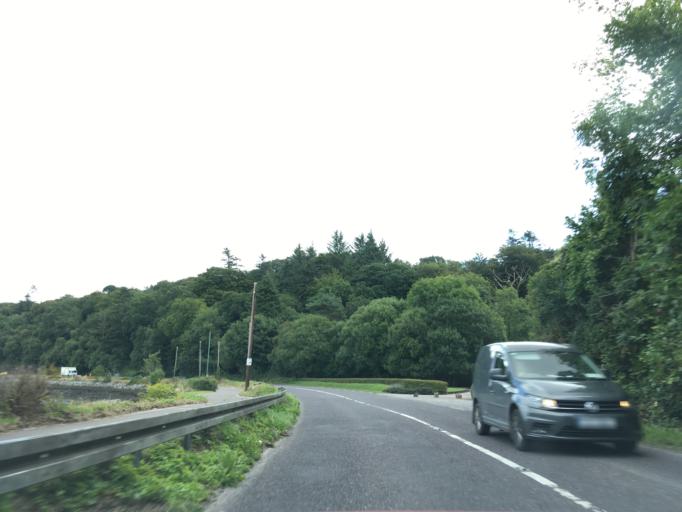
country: IE
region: Munster
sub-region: County Cork
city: Crosshaven
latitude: 51.8013
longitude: -8.3285
